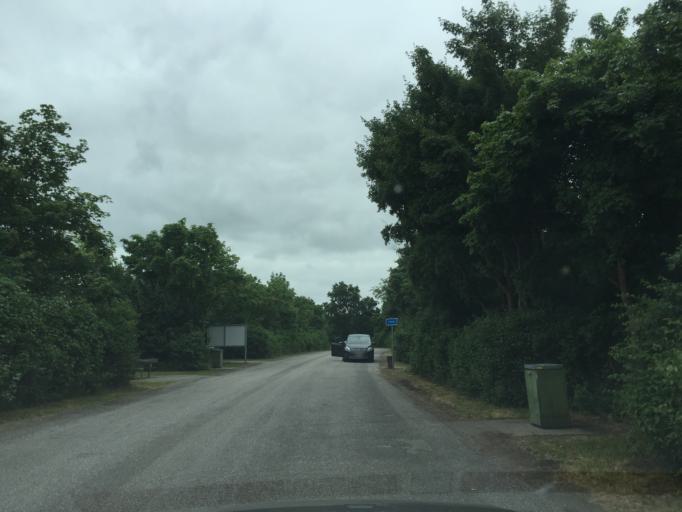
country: DK
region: South Denmark
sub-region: Esbjerg Kommune
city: Ribe
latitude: 55.3023
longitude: 8.7434
